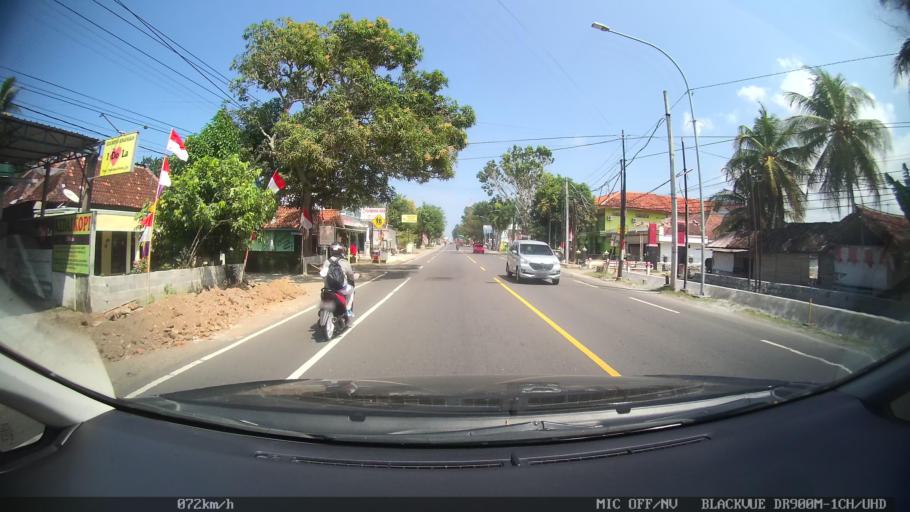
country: ID
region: Daerah Istimewa Yogyakarta
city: Srandakan
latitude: -7.8873
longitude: 110.0848
